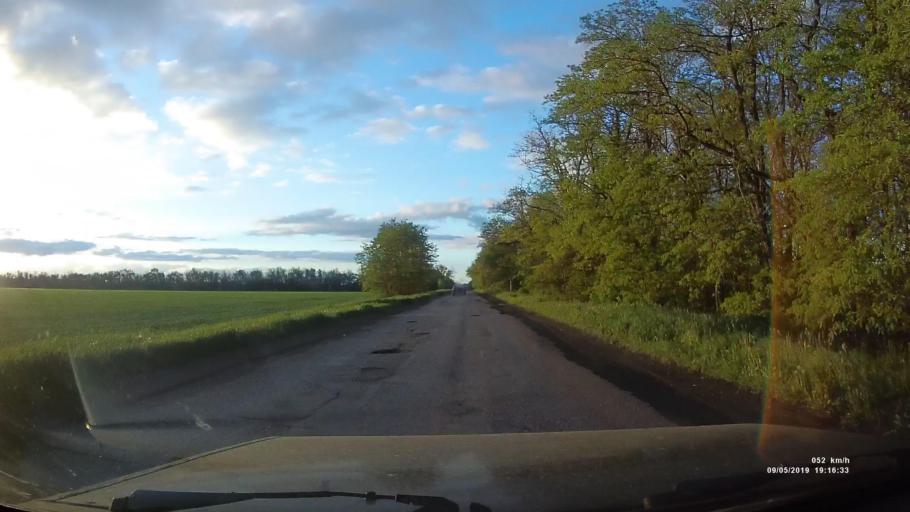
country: RU
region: Krasnodarskiy
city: Kanelovskaya
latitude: 46.7786
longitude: 39.2116
